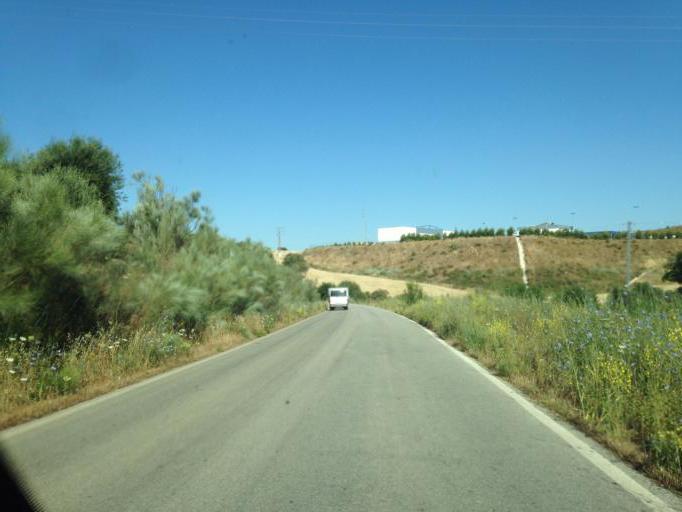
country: ES
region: Andalusia
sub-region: Provincia de Malaga
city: Casabermeja
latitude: 36.9011
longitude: -4.4536
